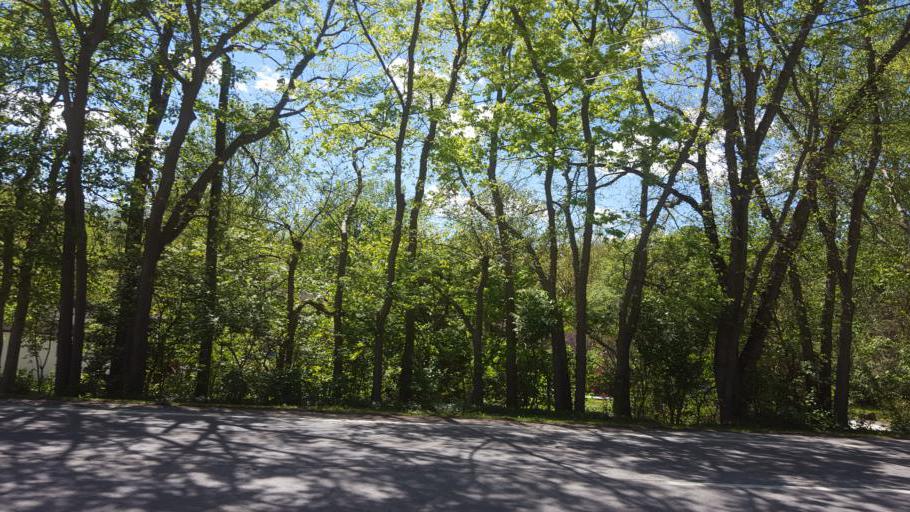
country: US
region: Ohio
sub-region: Franklin County
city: Dublin
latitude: 40.1459
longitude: -83.1215
